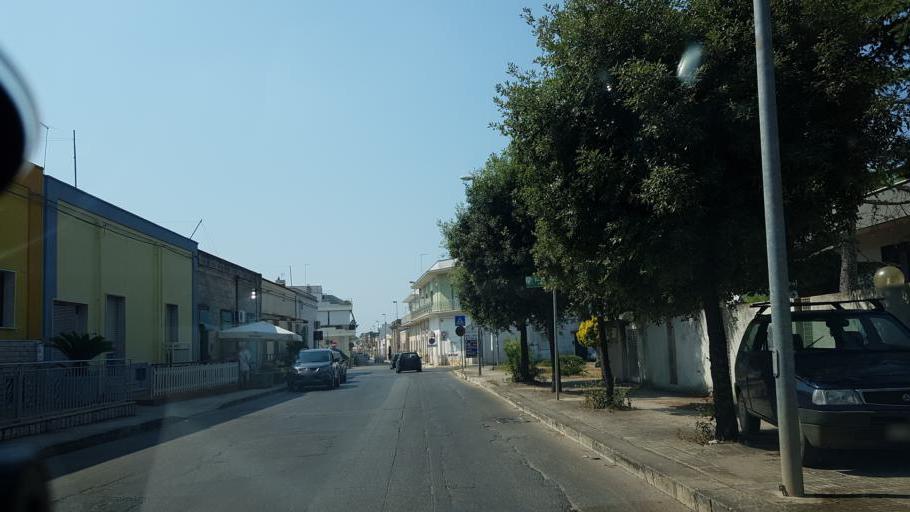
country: IT
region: Apulia
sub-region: Provincia di Taranto
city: Maruggio
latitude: 40.3266
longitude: 17.5732
